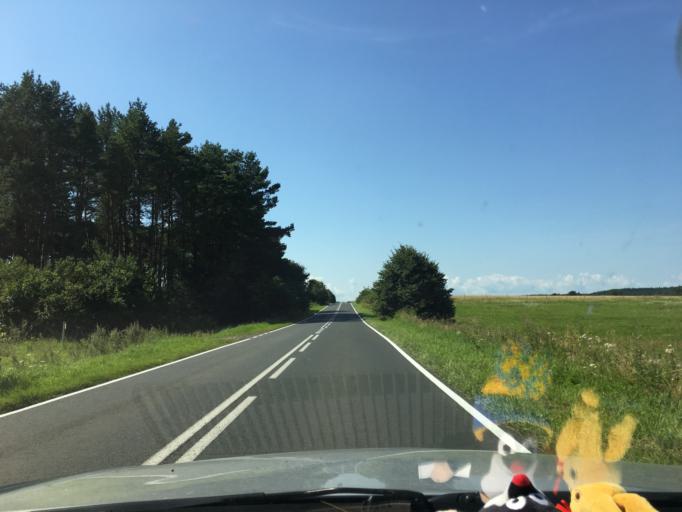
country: PL
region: West Pomeranian Voivodeship
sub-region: Powiat kamienski
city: Wolin
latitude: 53.9738
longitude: 14.6267
